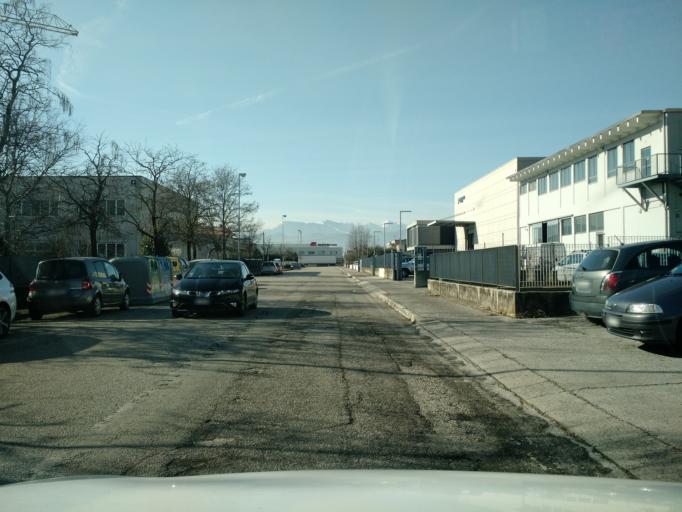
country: IT
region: Veneto
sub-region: Provincia di Vicenza
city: Thiene
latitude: 45.6820
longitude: 11.4734
